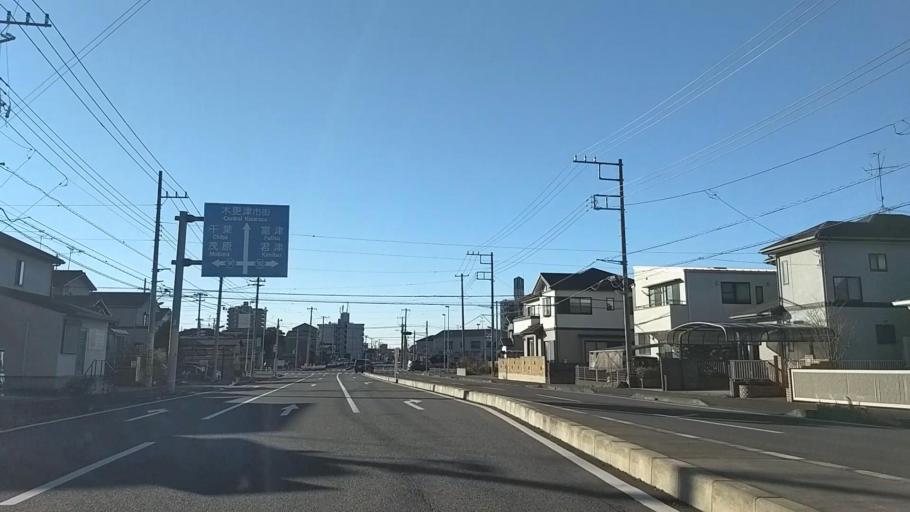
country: JP
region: Chiba
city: Kisarazu
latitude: 35.3871
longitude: 139.9203
